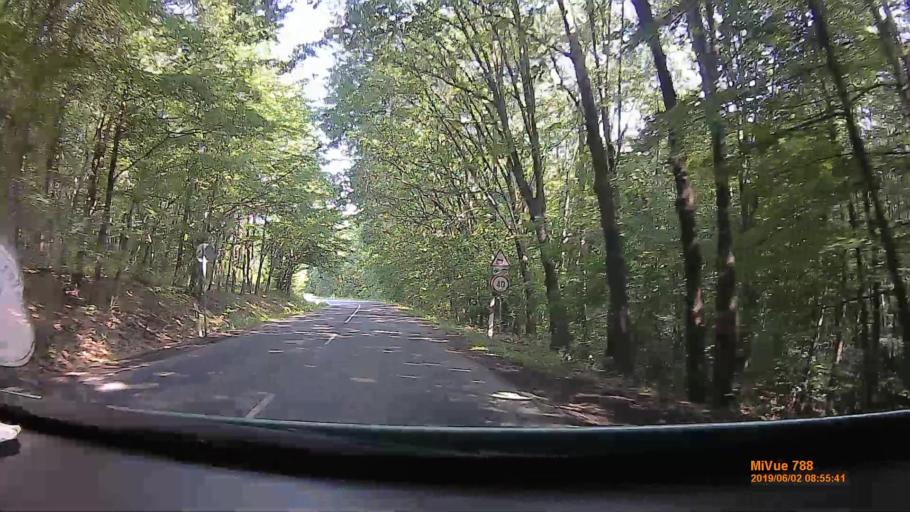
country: HU
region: Borsod-Abauj-Zemplen
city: Sajobabony
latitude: 48.1553
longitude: 20.6596
